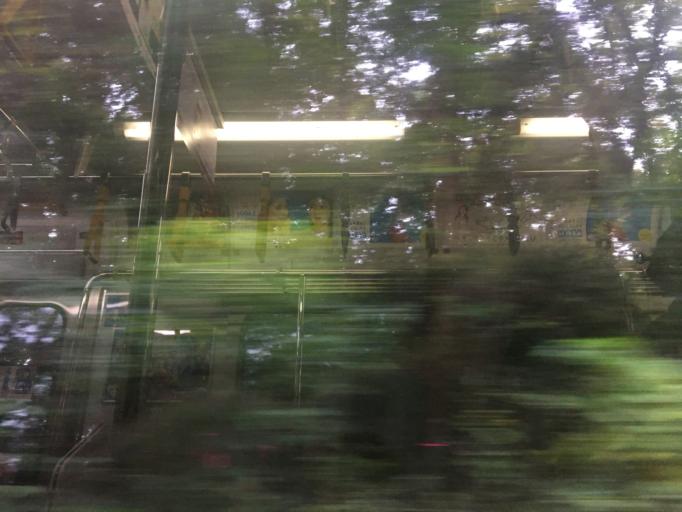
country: JP
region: Saitama
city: Sakado
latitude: 35.9051
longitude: 139.3830
